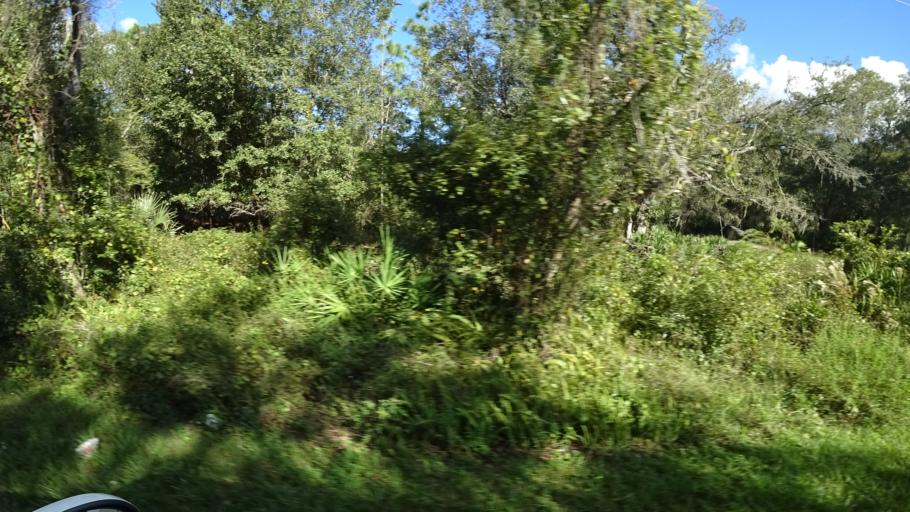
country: US
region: Florida
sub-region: Sarasota County
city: Lake Sarasota
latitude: 27.3228
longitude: -82.2693
